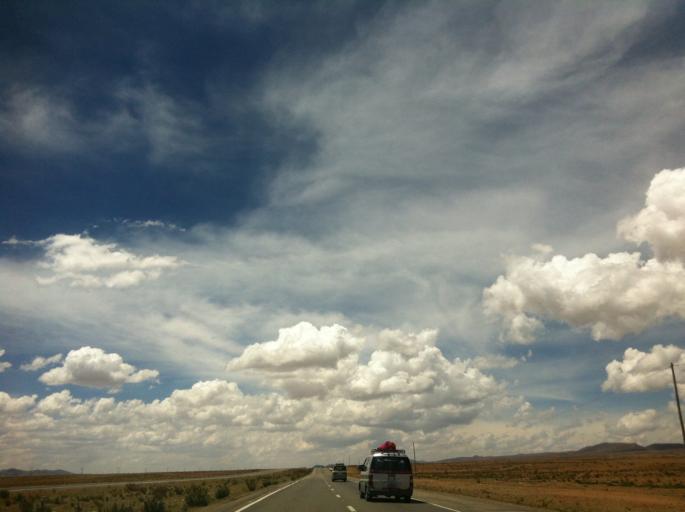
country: BO
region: La Paz
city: Patacamaya
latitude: -17.0841
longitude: -68.0147
